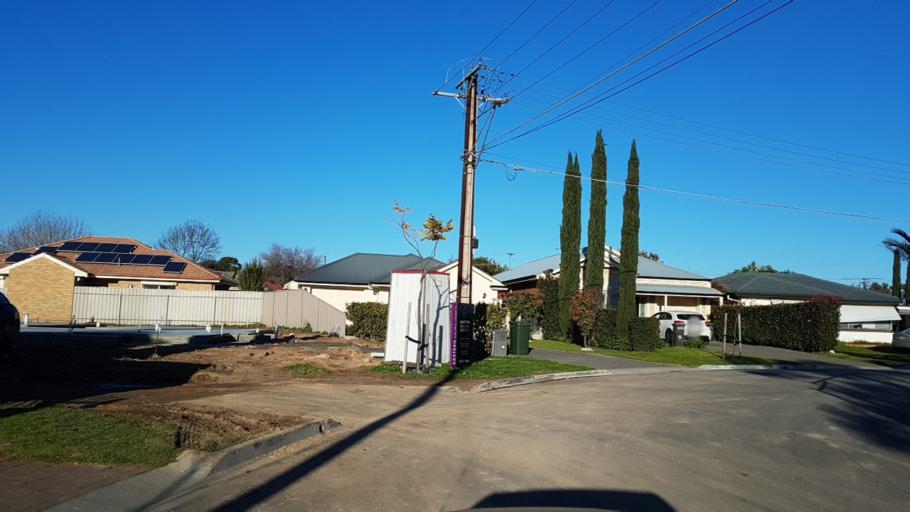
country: AU
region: South Australia
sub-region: Campbelltown
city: Campbelltown
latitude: -34.8784
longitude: 138.6554
